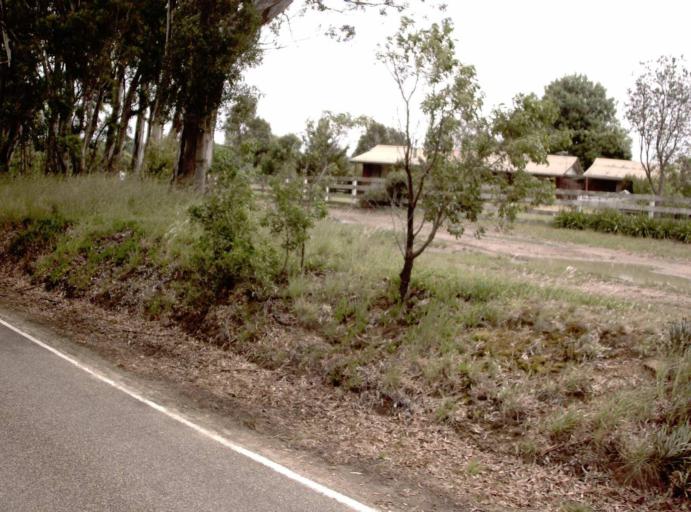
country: AU
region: Victoria
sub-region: Wellington
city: Sale
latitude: -37.9303
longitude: 147.0932
